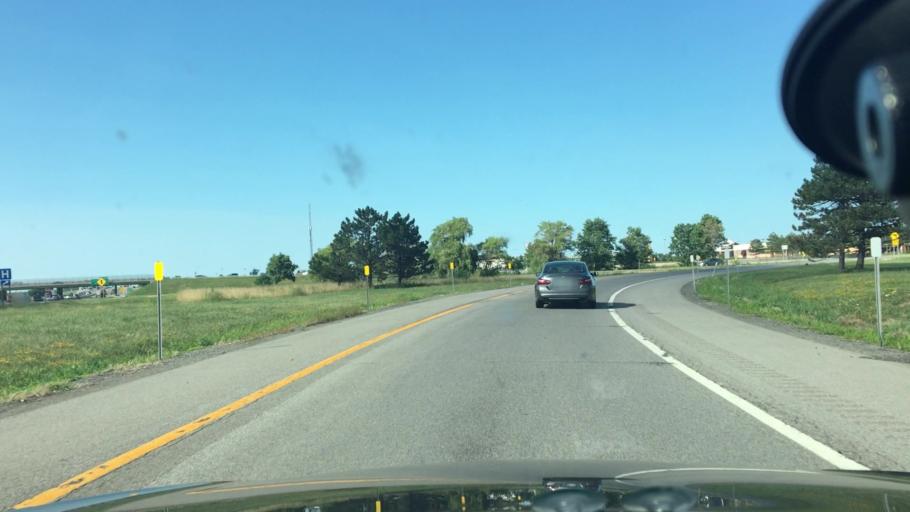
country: US
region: New York
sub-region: Erie County
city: Cheektowaga
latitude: 42.9058
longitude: -78.7664
